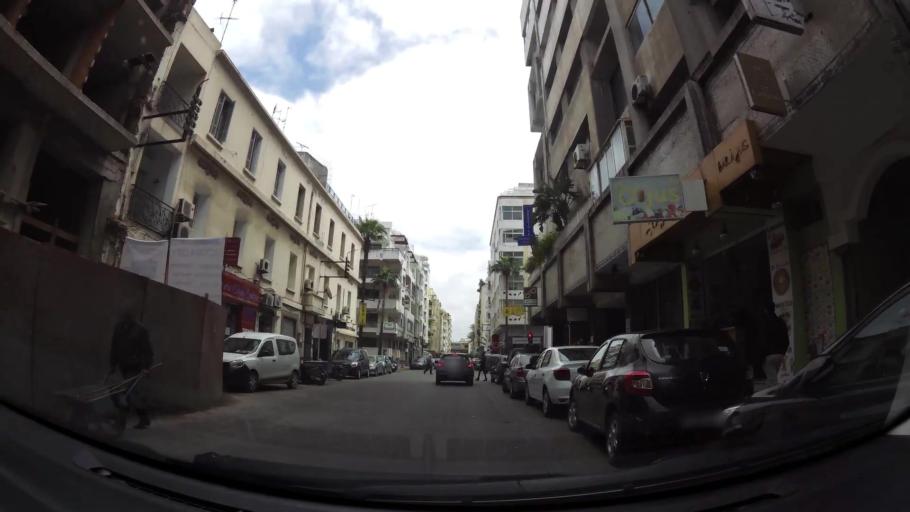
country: MA
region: Grand Casablanca
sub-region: Casablanca
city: Casablanca
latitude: 33.5897
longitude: -7.6298
